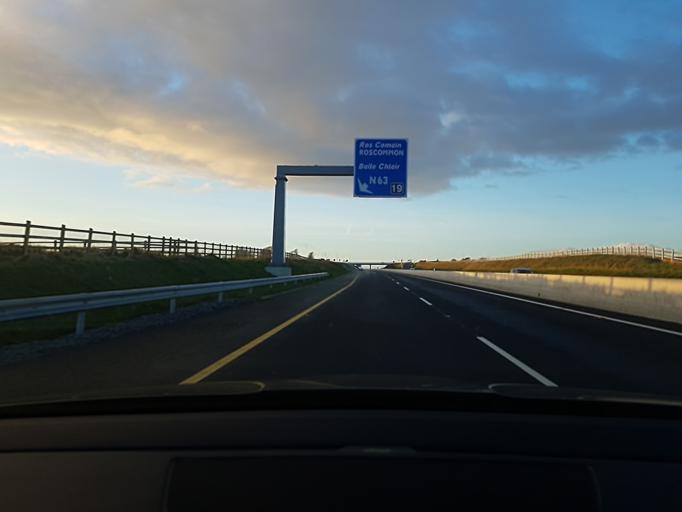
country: IE
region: Connaught
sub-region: County Galway
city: Tuam
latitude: 53.3993
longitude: -8.8117
